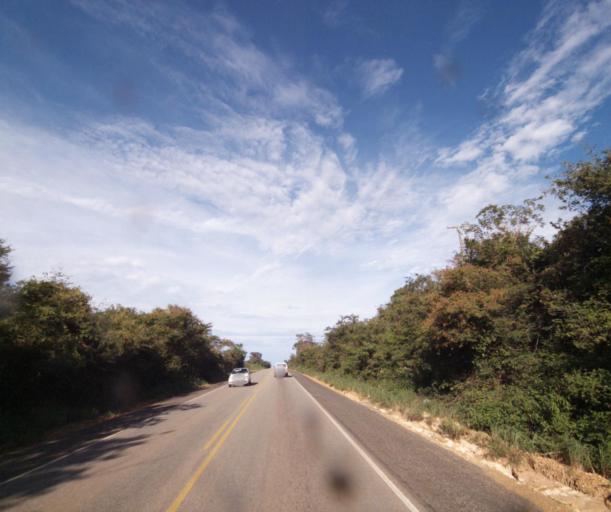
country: BR
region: Bahia
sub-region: Caetite
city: Caetite
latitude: -14.0814
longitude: -42.5583
